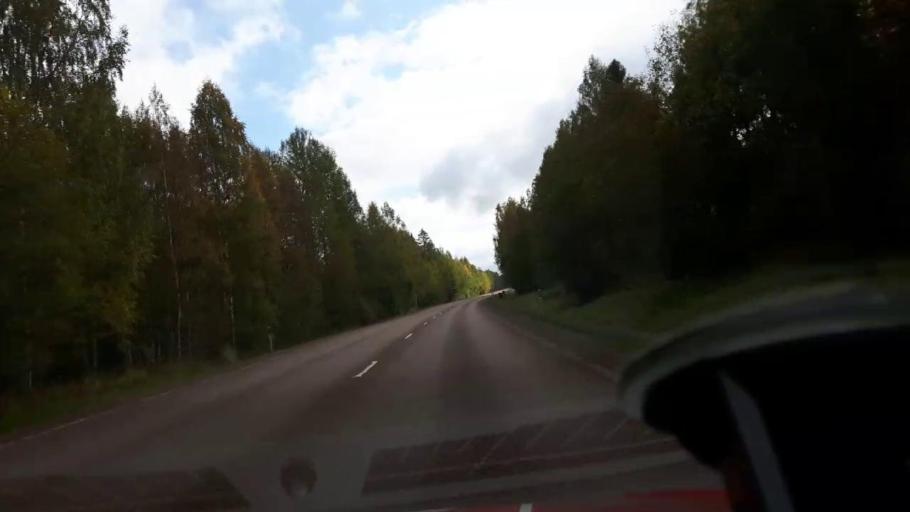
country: SE
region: Gaevleborg
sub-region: Ljusdals Kommun
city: Jaervsoe
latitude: 61.6432
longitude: 16.2239
